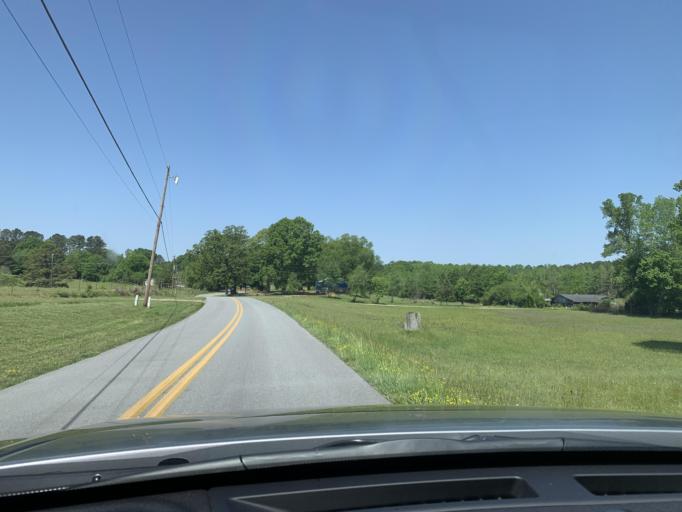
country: US
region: Georgia
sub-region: Polk County
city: Cedartown
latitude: 33.9854
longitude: -85.2234
